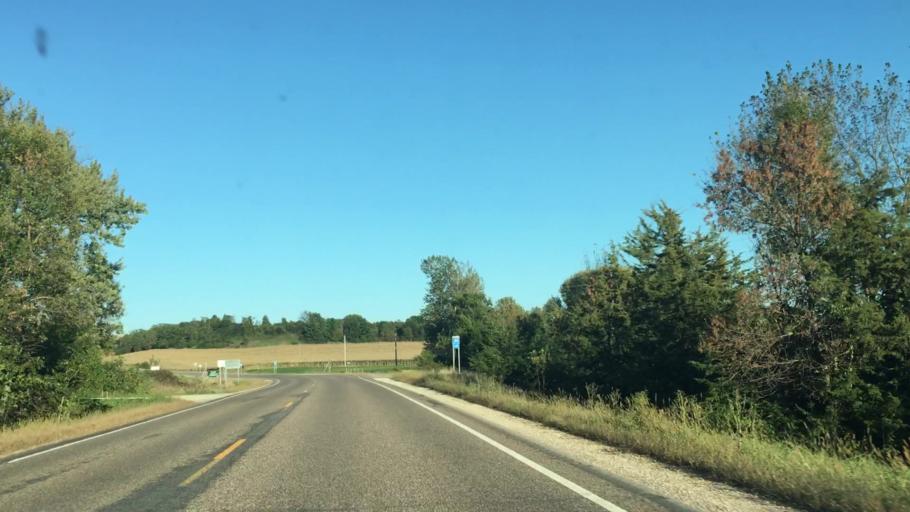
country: US
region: Minnesota
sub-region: Fillmore County
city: Chatfield
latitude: 43.8543
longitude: -92.1120
